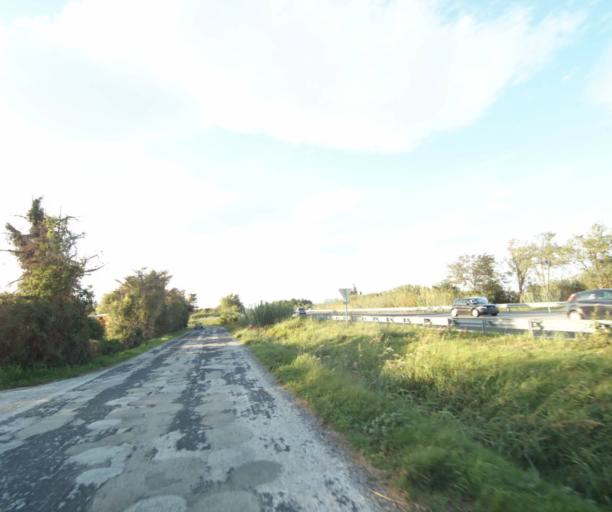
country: FR
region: Languedoc-Roussillon
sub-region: Departement des Pyrenees-Orientales
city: Elne
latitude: 42.5825
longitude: 2.9876
